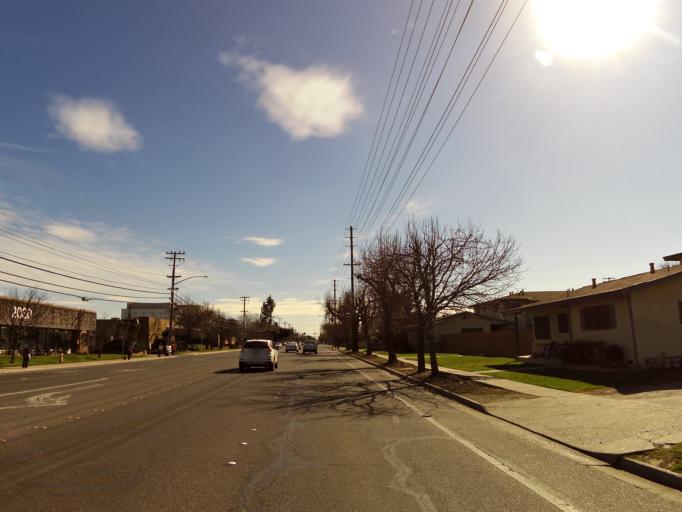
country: US
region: California
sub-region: Stanislaus County
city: Modesto
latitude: 37.6739
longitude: -120.9759
